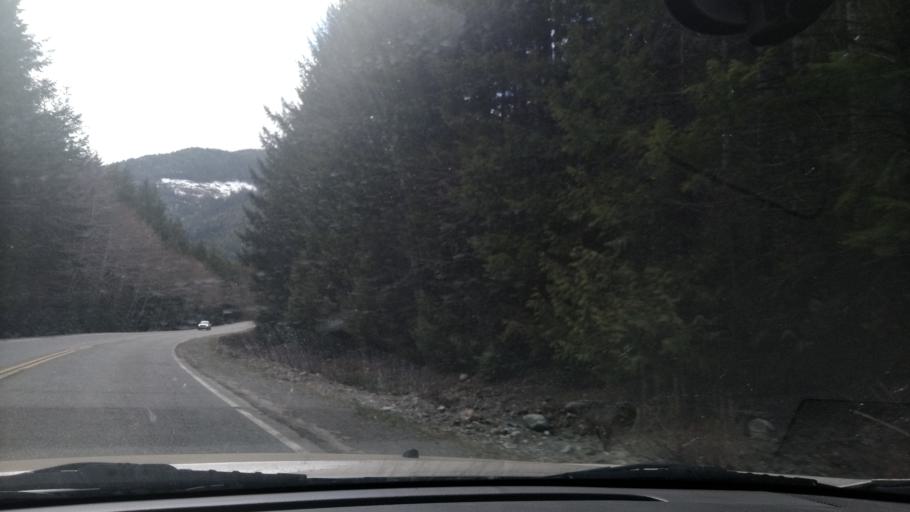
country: CA
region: British Columbia
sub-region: Regional District of Alberni-Clayoquot
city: Tofino
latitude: 49.8320
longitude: -125.9682
